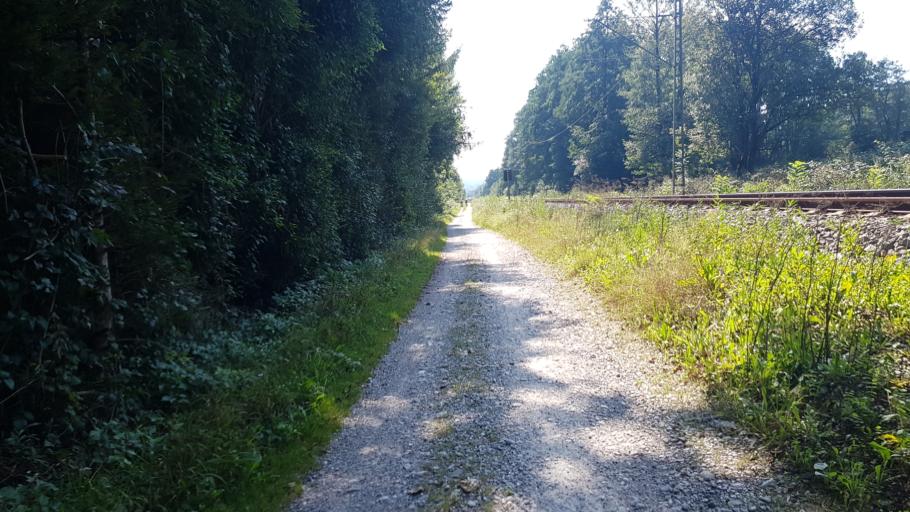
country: DE
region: Bavaria
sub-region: Upper Bavaria
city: Herrsching am Ammersee
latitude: 48.0182
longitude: 11.1728
